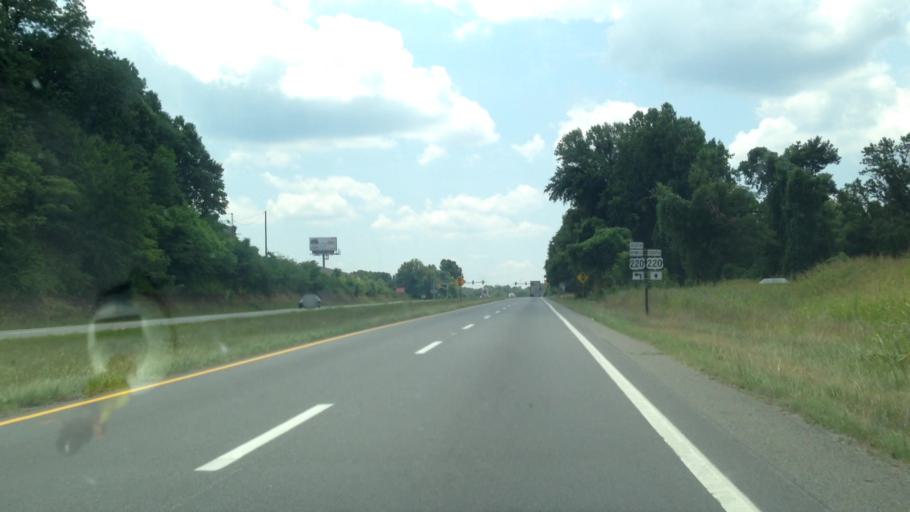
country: US
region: Virginia
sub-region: Henry County
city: Chatmoss
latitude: 36.5904
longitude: -79.8631
